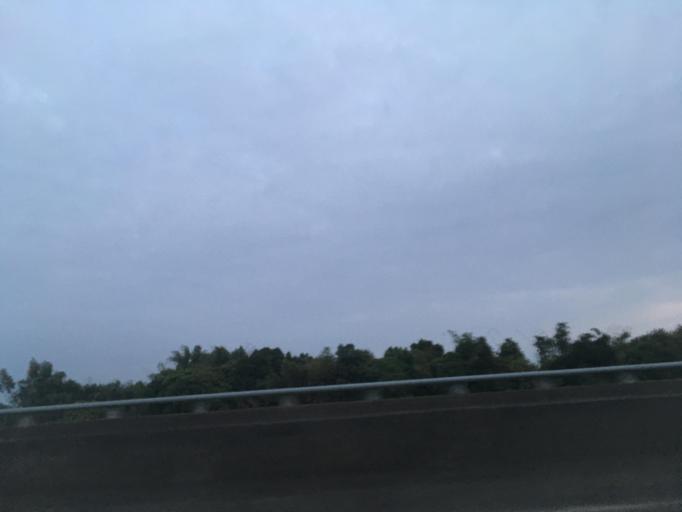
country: TW
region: Taiwan
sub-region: Chiayi
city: Jiayi Shi
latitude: 23.5925
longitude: 120.4651
